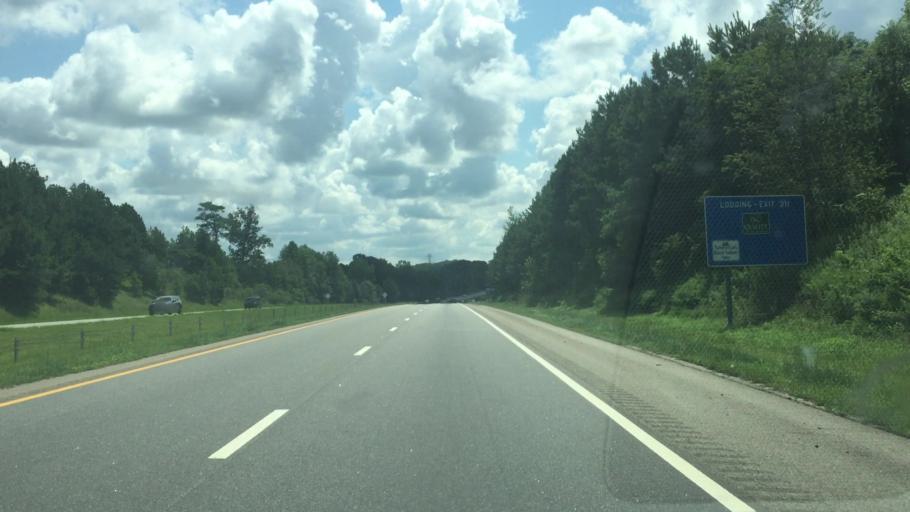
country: US
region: North Carolina
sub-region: Richmond County
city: Cordova
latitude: 34.9195
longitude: -79.8078
